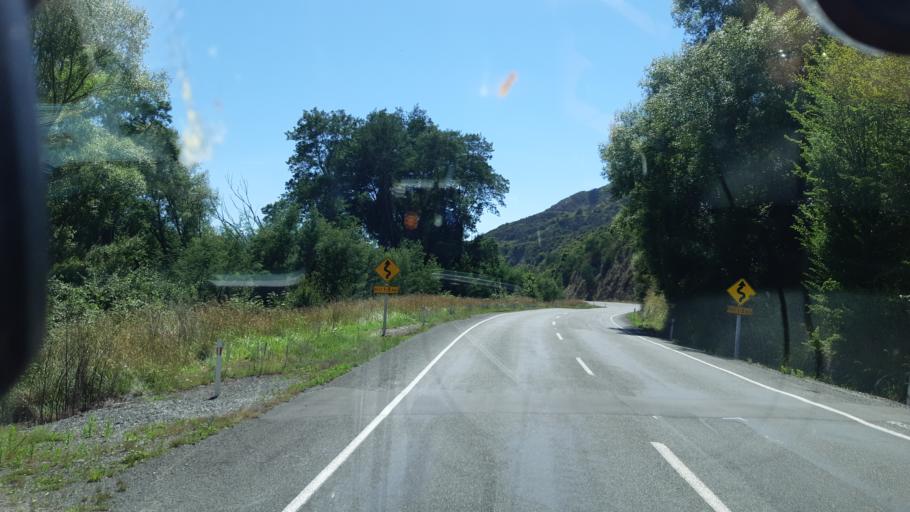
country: NZ
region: Canterbury
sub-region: Kaikoura District
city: Kaikoura
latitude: -42.6345
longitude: 173.3490
